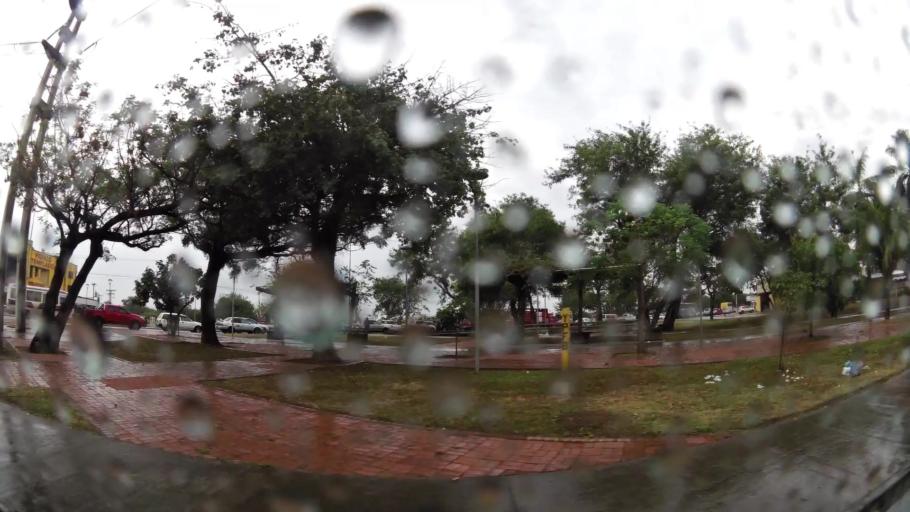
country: BO
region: Santa Cruz
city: Santa Cruz de la Sierra
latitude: -17.7754
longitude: -63.1475
